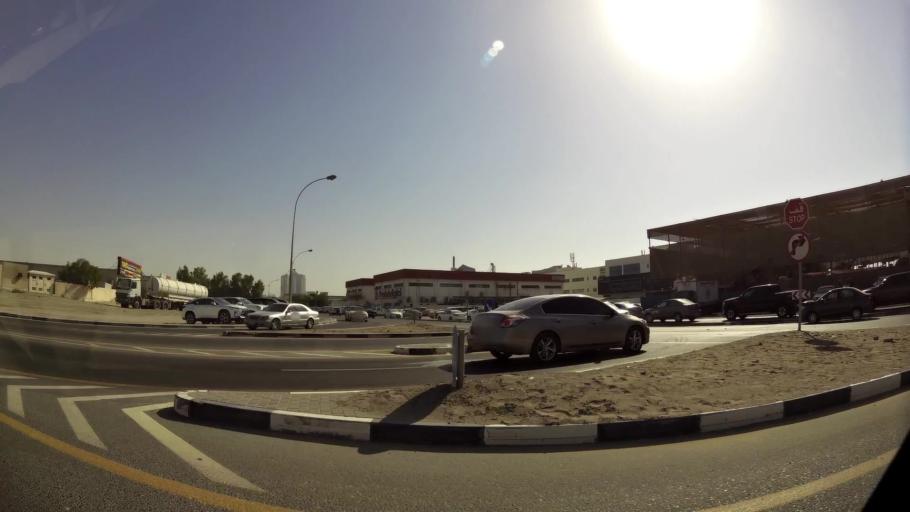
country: AE
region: Dubai
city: Dubai
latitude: 25.1290
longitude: 55.2129
